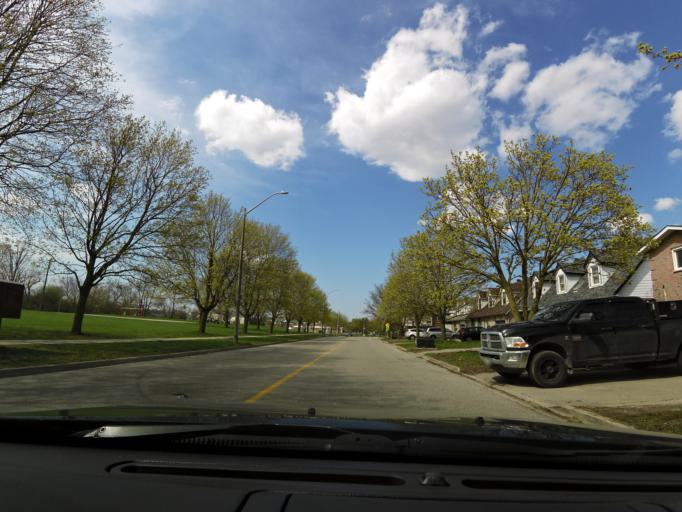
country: CA
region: Ontario
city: Cambridge
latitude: 43.3941
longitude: -80.3777
